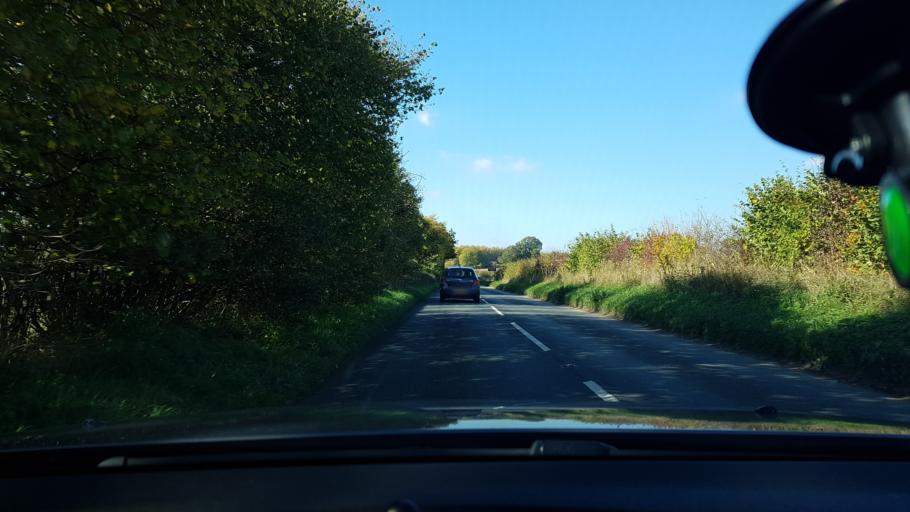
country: GB
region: England
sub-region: Wiltshire
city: Ramsbury
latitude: 51.4395
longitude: -1.5739
